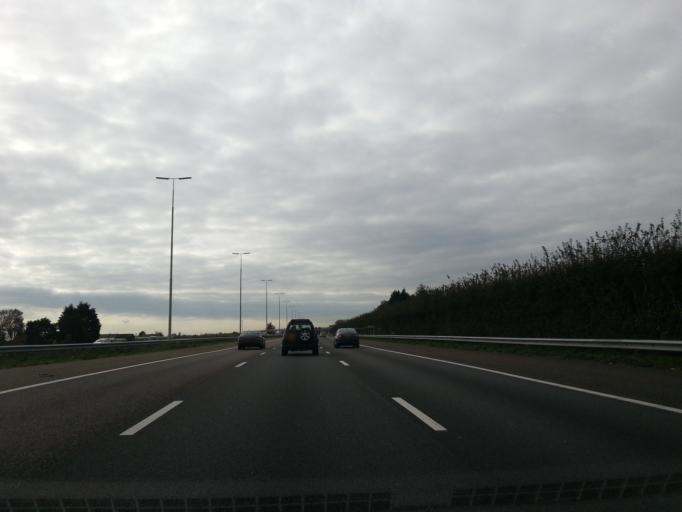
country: NL
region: South Holland
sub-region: Gemeente Voorschoten
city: Voorschoten
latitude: 52.1030
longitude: 4.4493
